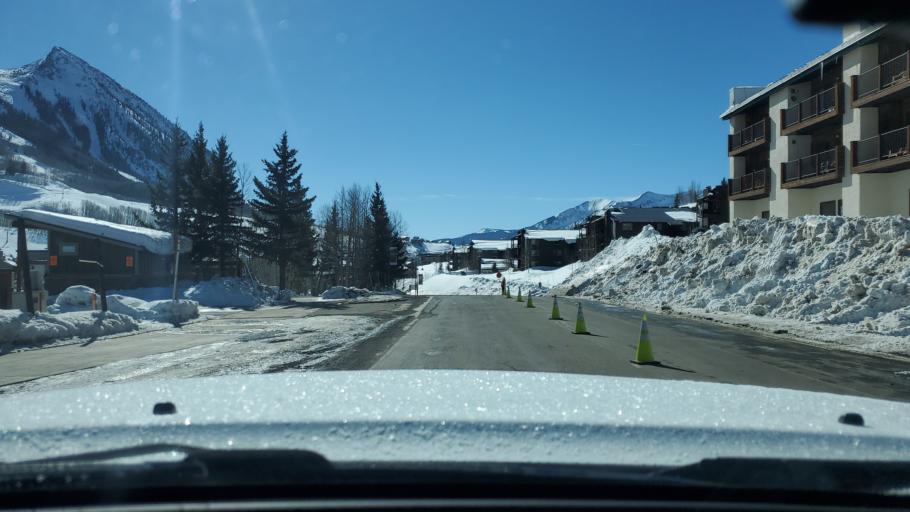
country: US
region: Colorado
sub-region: Gunnison County
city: Crested Butte
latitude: 38.9036
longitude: -106.9701
